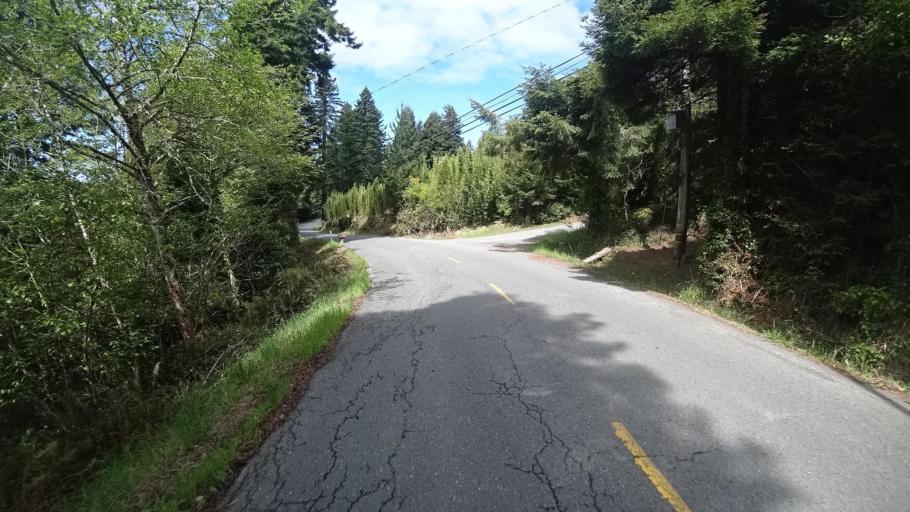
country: US
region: California
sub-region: Humboldt County
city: Bayside
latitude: 40.8666
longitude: -124.0494
